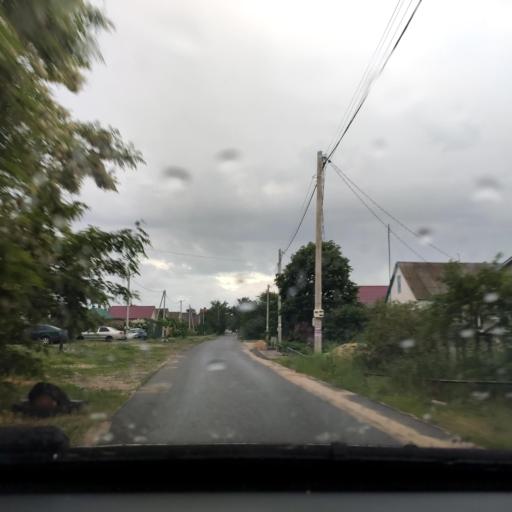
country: RU
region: Voronezj
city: Podgornoye
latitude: 51.7916
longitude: 39.1526
